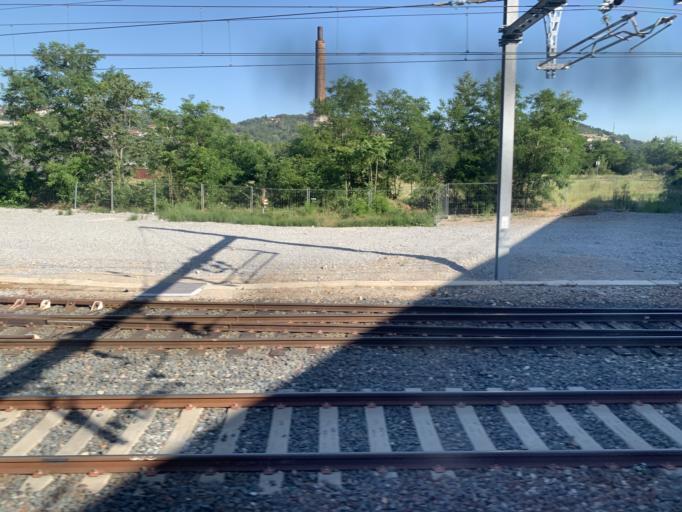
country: FR
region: Rhone-Alpes
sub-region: Departement du Rhone
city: Givors
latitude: 45.5861
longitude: 4.7679
